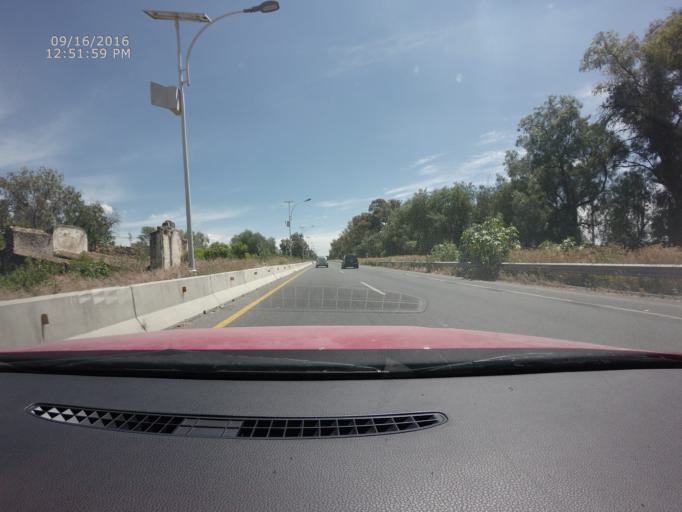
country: MX
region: Queretaro
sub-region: Colon
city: Purisima de Cubos (La Purisima)
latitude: 20.6165
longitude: -100.1495
